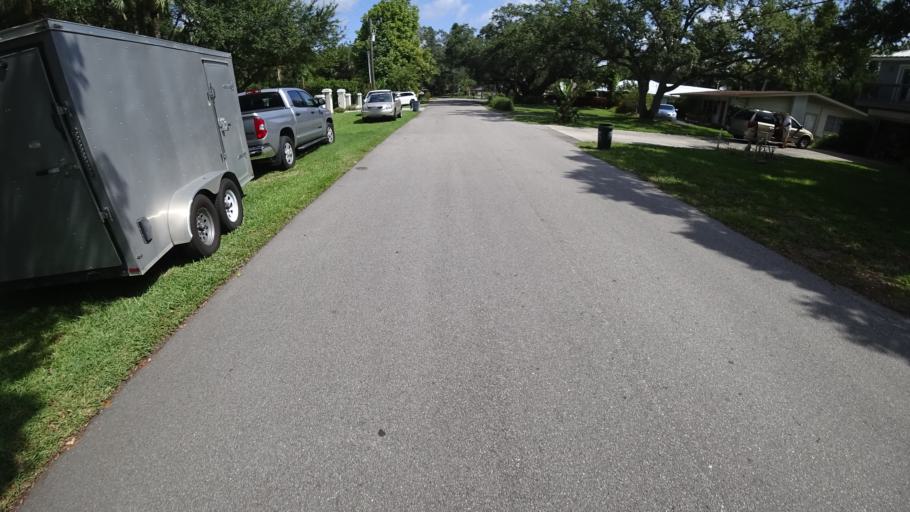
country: US
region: Florida
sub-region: Manatee County
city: Whitfield
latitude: 27.3955
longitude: -82.5675
